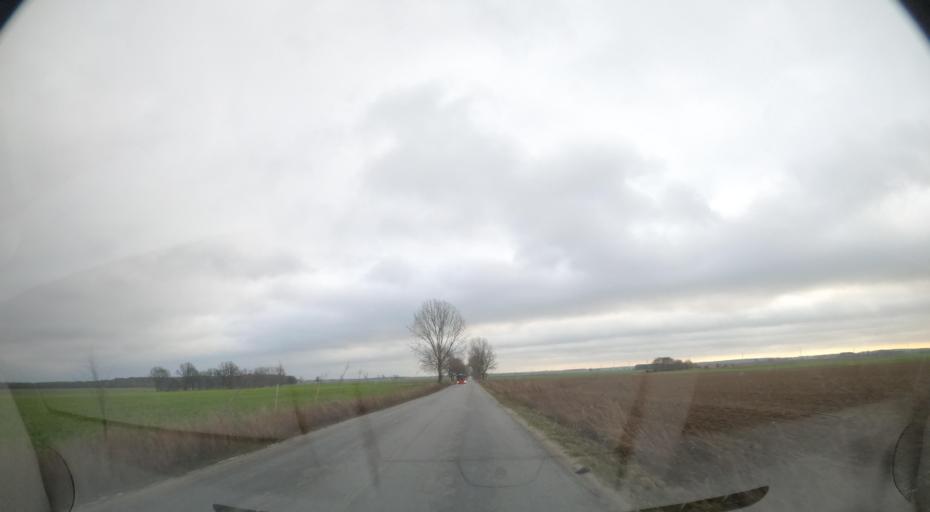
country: PL
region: Kujawsko-Pomorskie
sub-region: Powiat nakielski
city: Sadki
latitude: 53.2117
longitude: 17.3583
